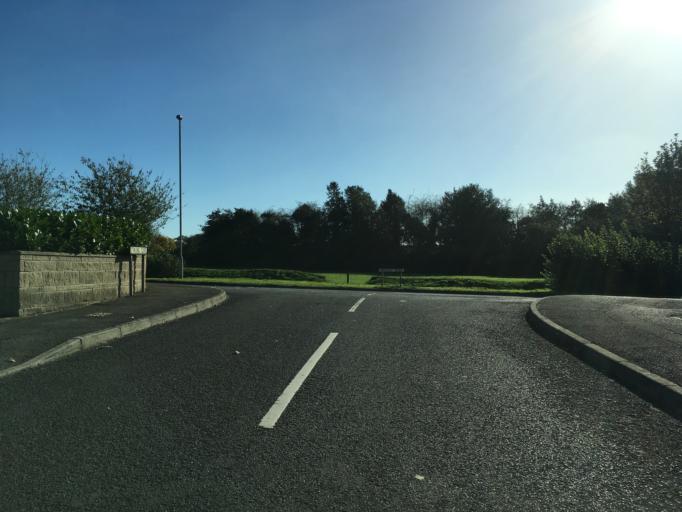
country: GB
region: England
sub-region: South Gloucestershire
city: Yate
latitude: 51.5502
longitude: -2.4201
